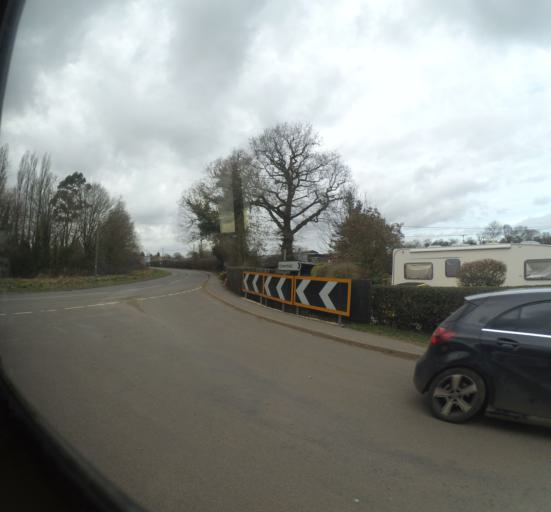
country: GB
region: England
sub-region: Warwickshire
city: Brandon
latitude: 52.4081
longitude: -1.3583
